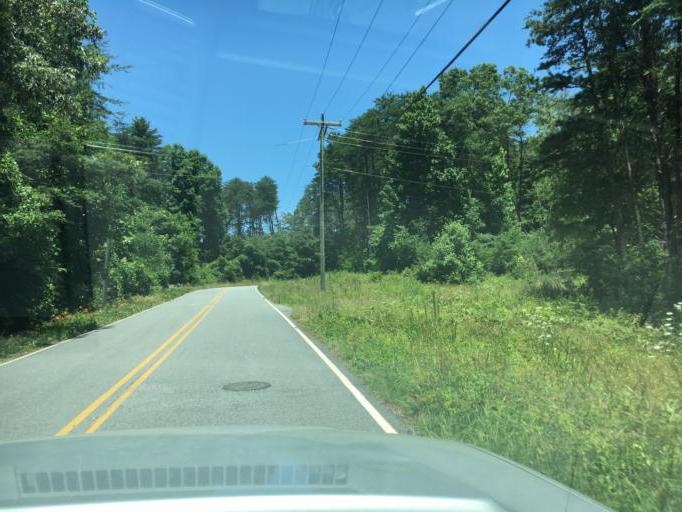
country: US
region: South Carolina
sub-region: Greenville County
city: Greer
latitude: 34.9593
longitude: -82.2224
